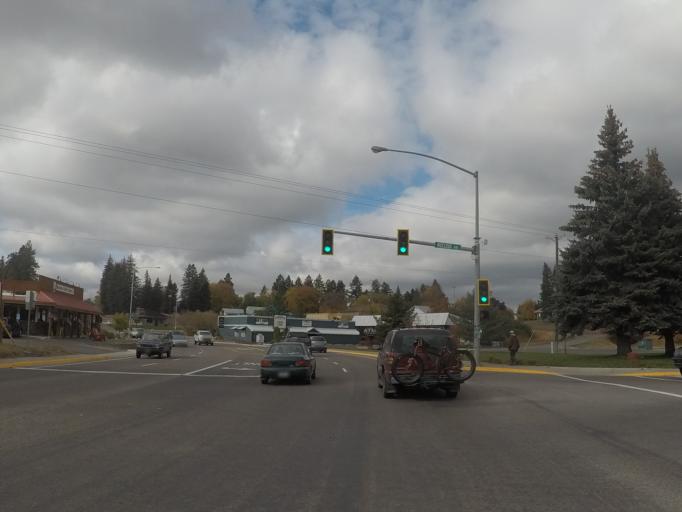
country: US
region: Montana
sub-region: Flathead County
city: Columbia Falls
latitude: 48.3703
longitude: -114.1812
